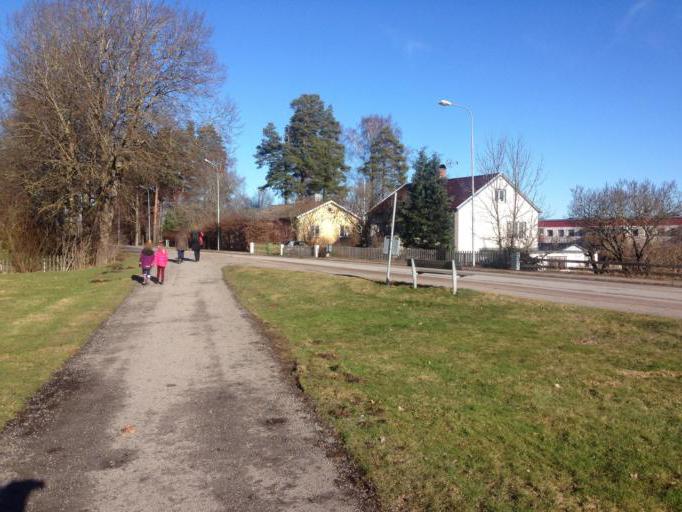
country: SE
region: Vaestra Goetaland
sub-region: Mariestads Kommun
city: Mariestad
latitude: 58.6943
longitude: 13.8117
